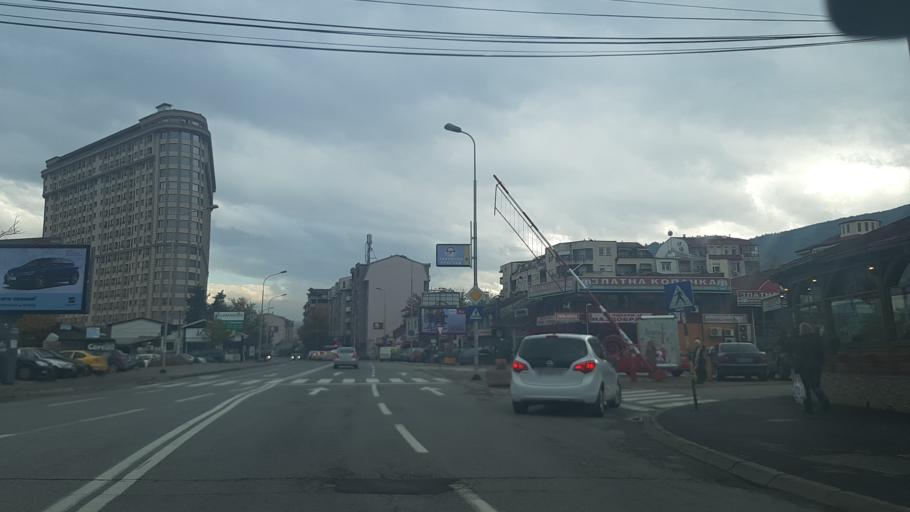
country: MK
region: Karpos
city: Skopje
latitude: 41.9870
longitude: 21.4370
